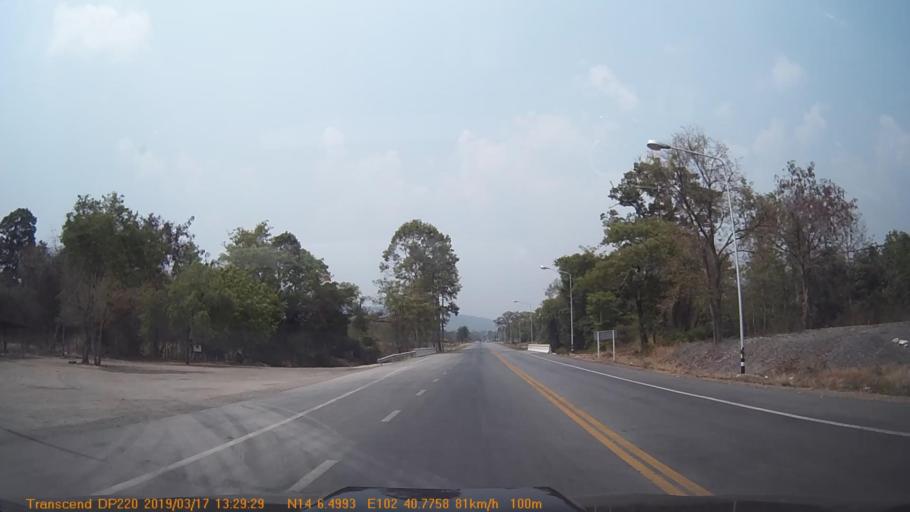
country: TH
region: Sa Kaeo
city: Ta Phraya
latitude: 14.1085
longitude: 102.6795
